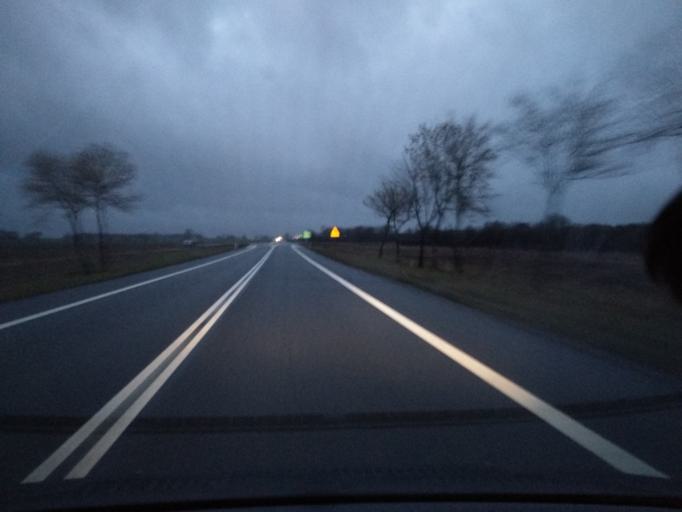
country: PL
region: Lower Silesian Voivodeship
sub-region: Powiat sredzki
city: Miekinia
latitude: 51.1619
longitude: 16.6876
